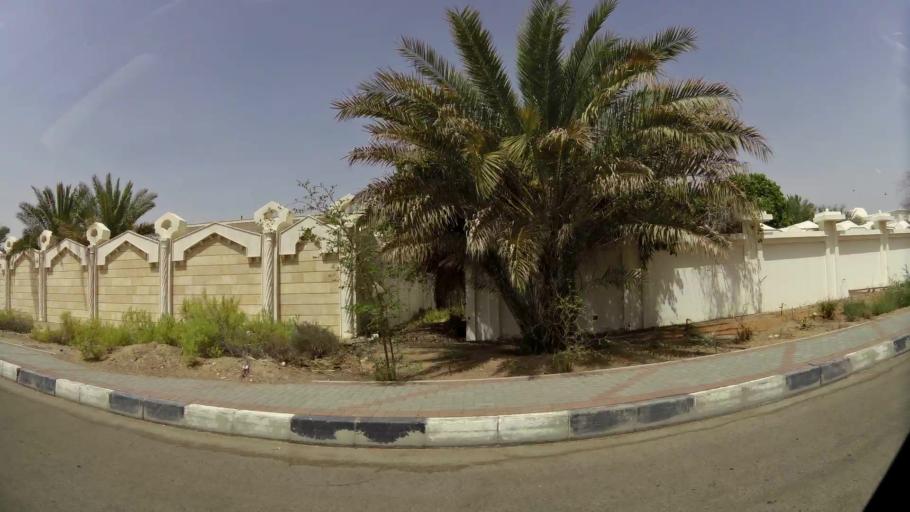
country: AE
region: Abu Dhabi
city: Al Ain
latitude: 24.1444
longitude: 55.6431
